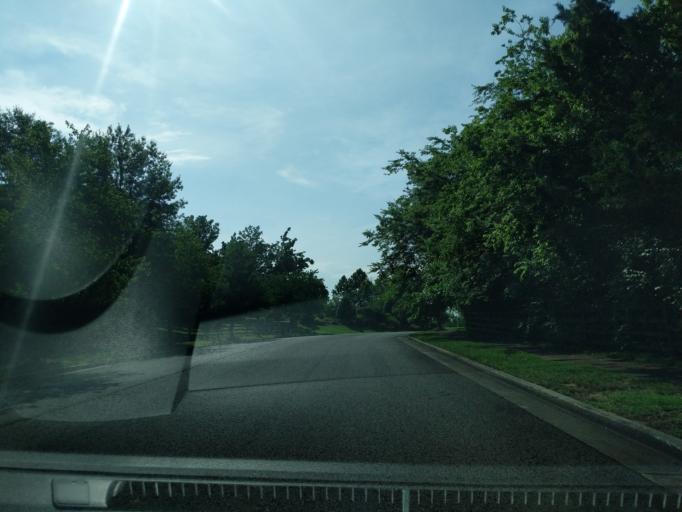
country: US
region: Tennessee
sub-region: Sumner County
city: Hendersonville
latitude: 36.3107
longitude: -86.6645
